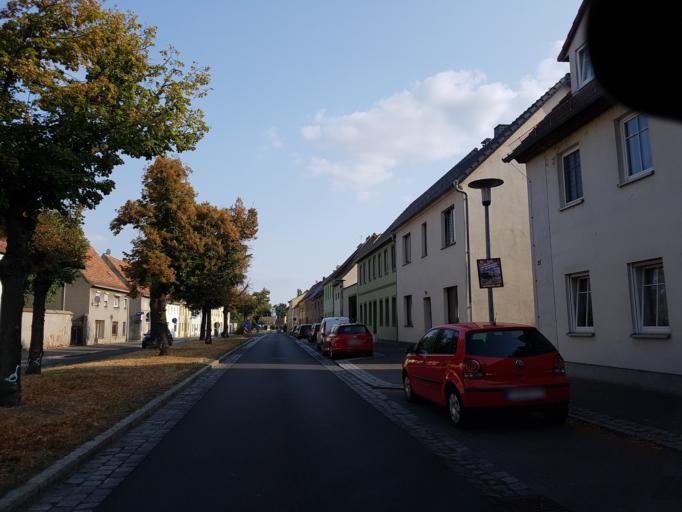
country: DE
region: Saxony
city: Dommitzsch
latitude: 51.6388
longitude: 12.8844
